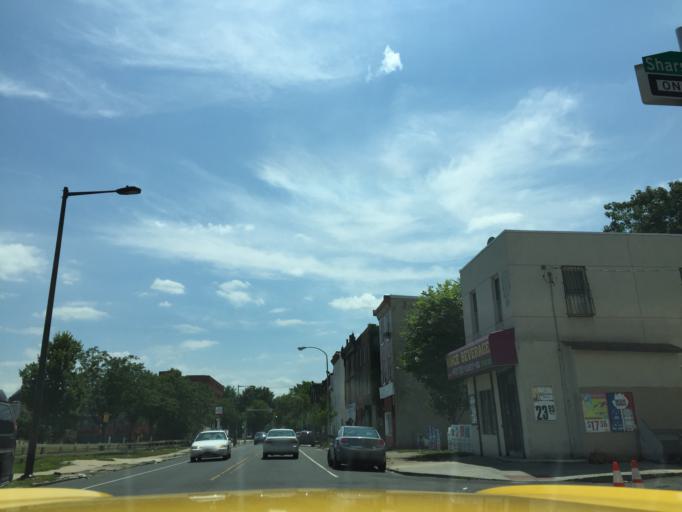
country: US
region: Pennsylvania
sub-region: Philadelphia County
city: Philadelphia
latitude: 39.9769
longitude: -75.1692
